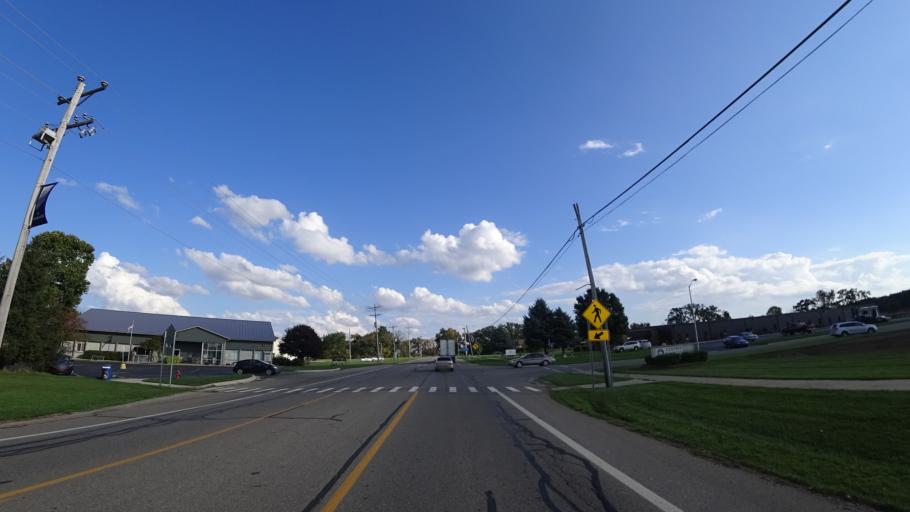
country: US
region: Michigan
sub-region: Saint Joseph County
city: Centreville
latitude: 41.9211
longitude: -85.5103
